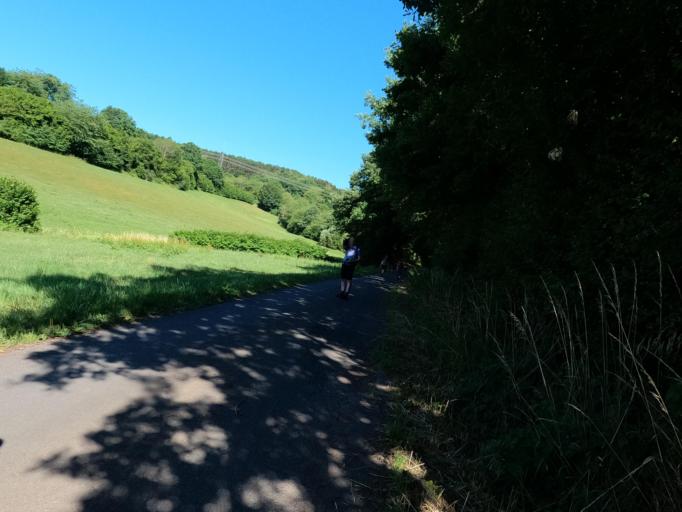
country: DE
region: Bavaria
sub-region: Regierungsbezirk Unterfranken
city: Zeitlofs
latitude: 50.3171
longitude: 9.6523
